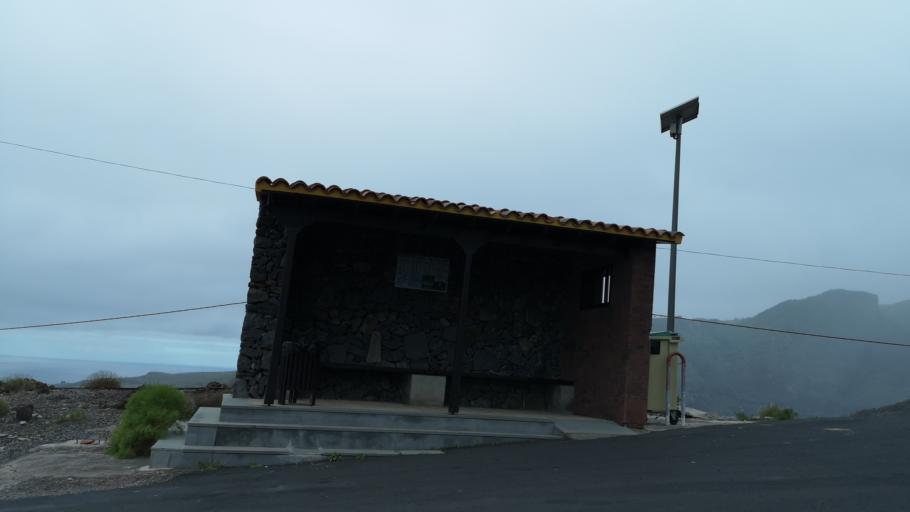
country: ES
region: Canary Islands
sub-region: Provincia de Santa Cruz de Tenerife
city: Alajero
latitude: 28.0622
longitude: -17.2033
